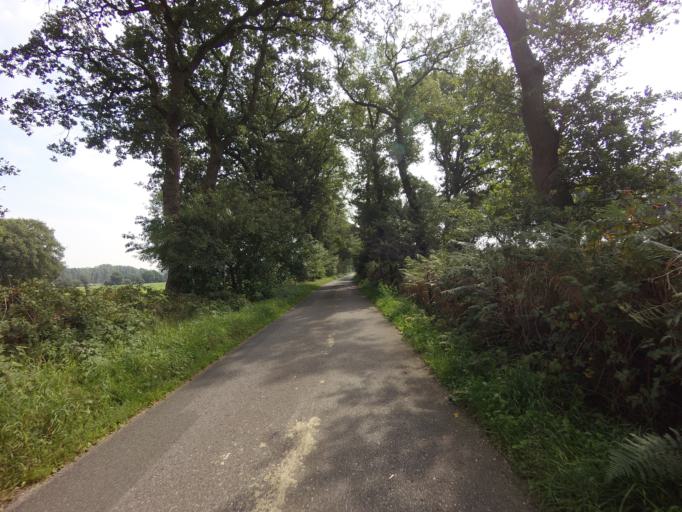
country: NL
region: Gelderland
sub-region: Gemeente Montferland
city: s-Heerenberg
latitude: 51.8888
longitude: 6.1706
